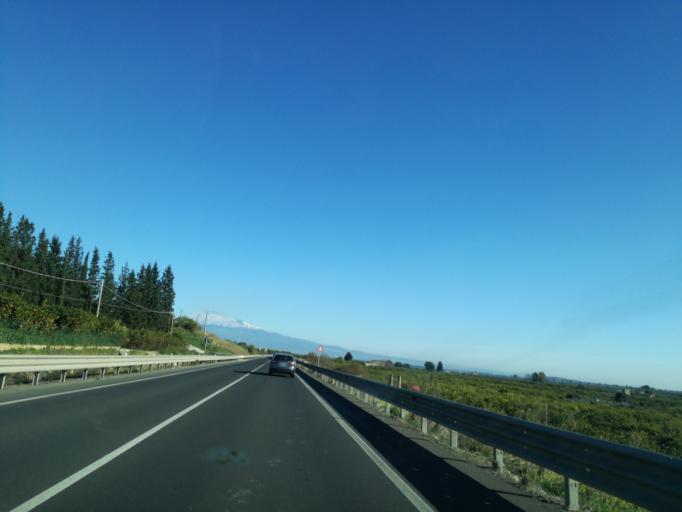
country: IT
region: Sicily
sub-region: Catania
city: Ramacca
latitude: 37.3729
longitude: 14.7263
